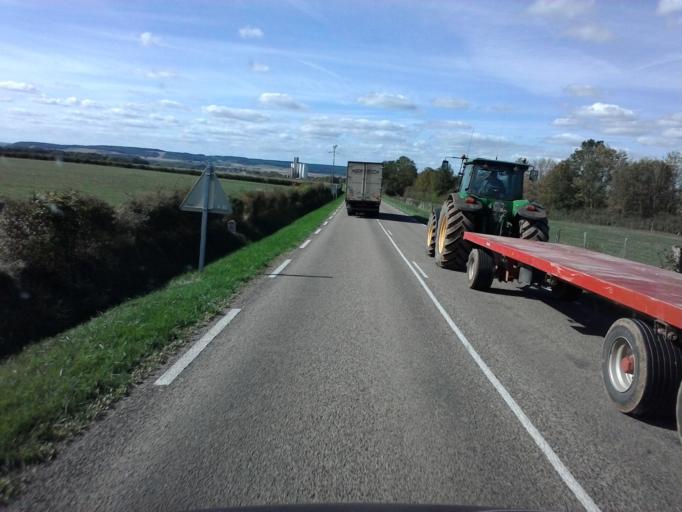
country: FR
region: Bourgogne
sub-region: Departement de la Cote-d'Or
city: Chatillon-sur-Seine
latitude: 47.9040
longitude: 4.6948
